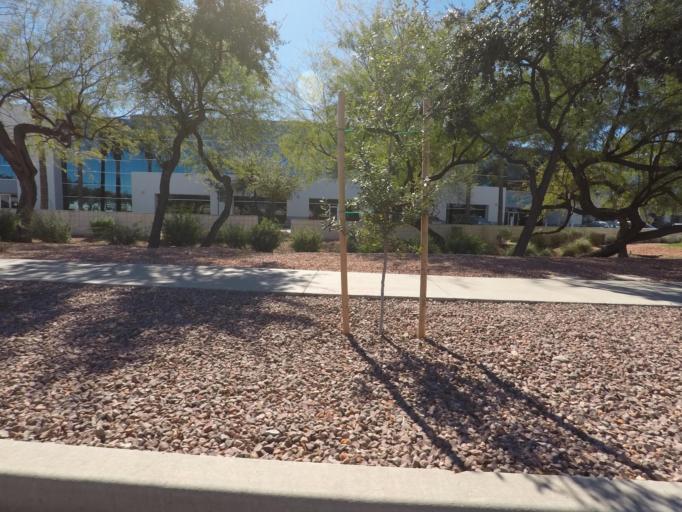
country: US
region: Arizona
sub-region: Maricopa County
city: Guadalupe
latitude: 33.4035
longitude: -111.9940
